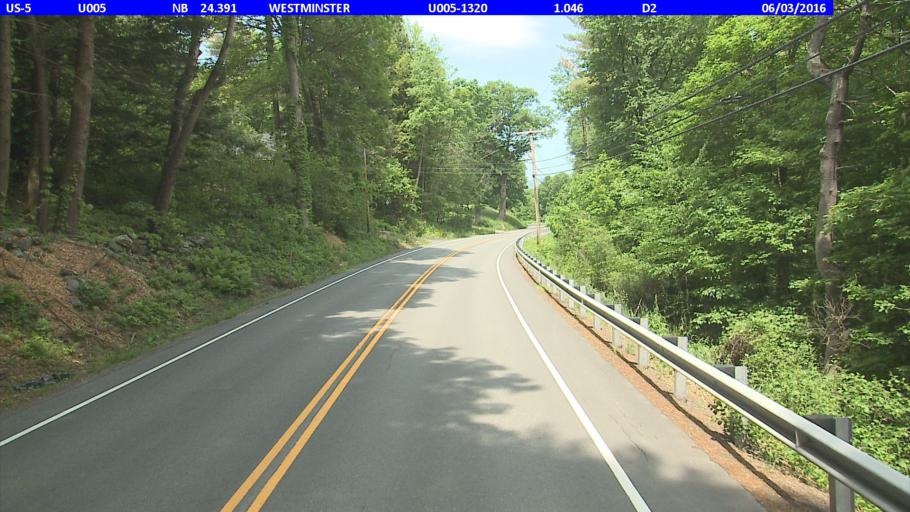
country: US
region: New Hampshire
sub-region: Cheshire County
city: Westmoreland
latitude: 43.0353
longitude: -72.4665
